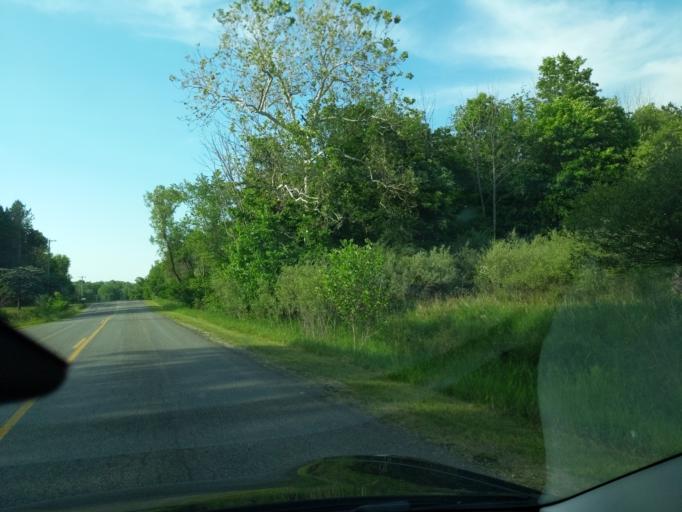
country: US
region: Michigan
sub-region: Barry County
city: Nashville
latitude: 42.6177
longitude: -85.1537
